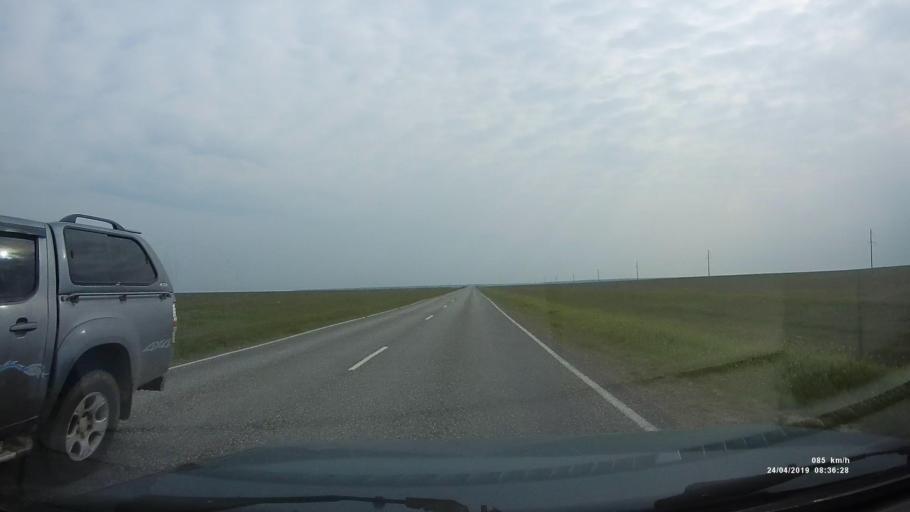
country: RU
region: Kalmykiya
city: Arshan'
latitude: 46.2048
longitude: 43.9349
